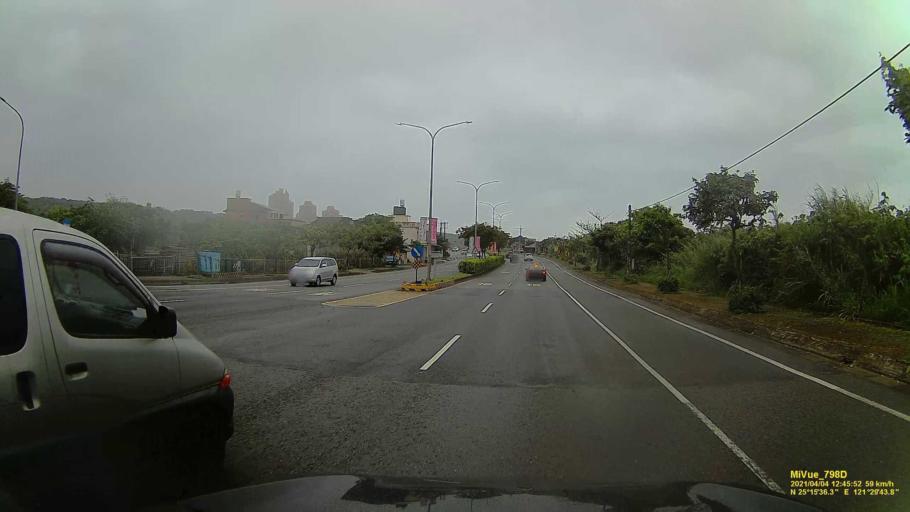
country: TW
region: Taipei
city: Taipei
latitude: 25.2601
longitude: 121.4952
